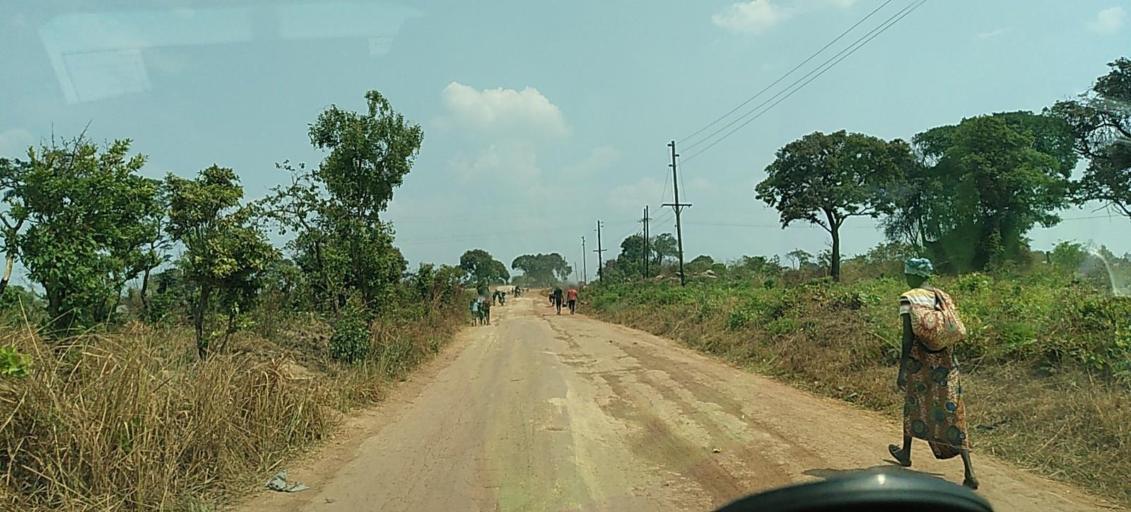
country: ZM
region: North-Western
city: Solwezi
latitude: -12.1174
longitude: 26.3678
